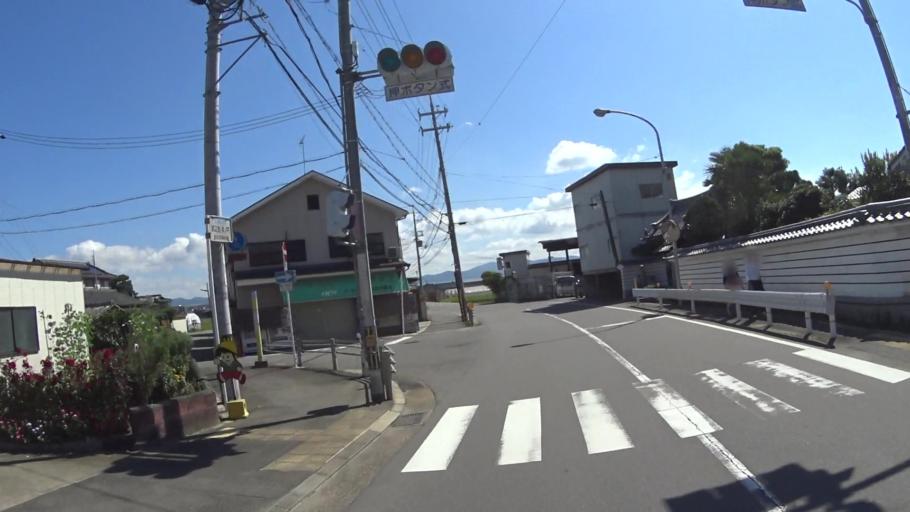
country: JP
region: Kyoto
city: Yawata
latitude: 34.8923
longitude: 135.7325
